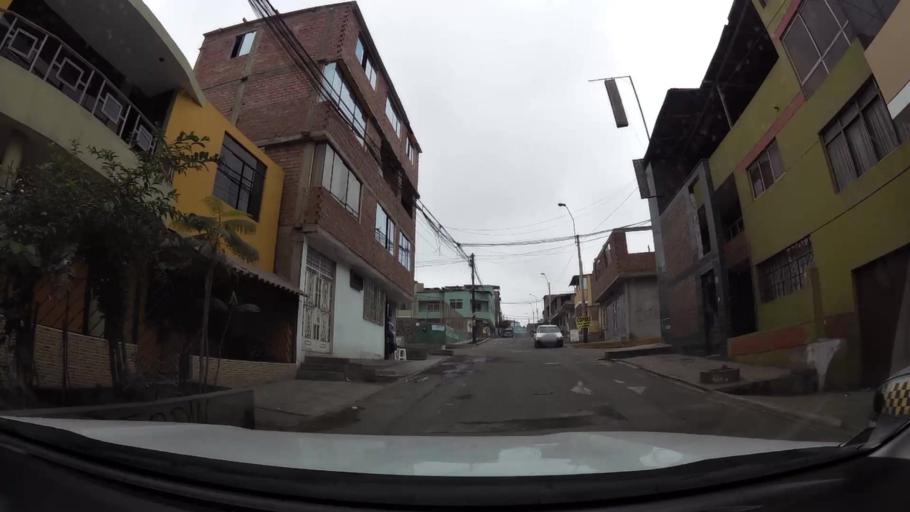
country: PE
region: Lima
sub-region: Lima
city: Surco
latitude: -12.1654
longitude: -76.9553
